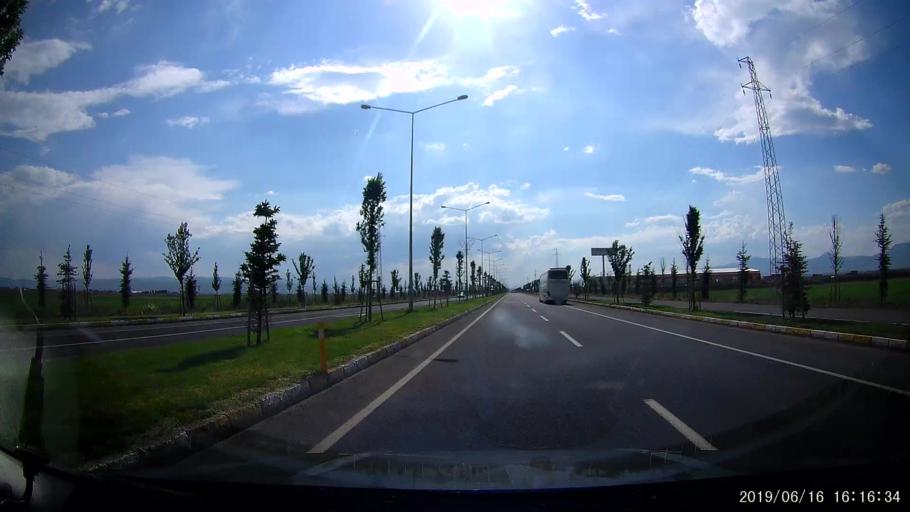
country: TR
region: Erzurum
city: Erzurum
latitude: 39.9629
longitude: 41.2048
